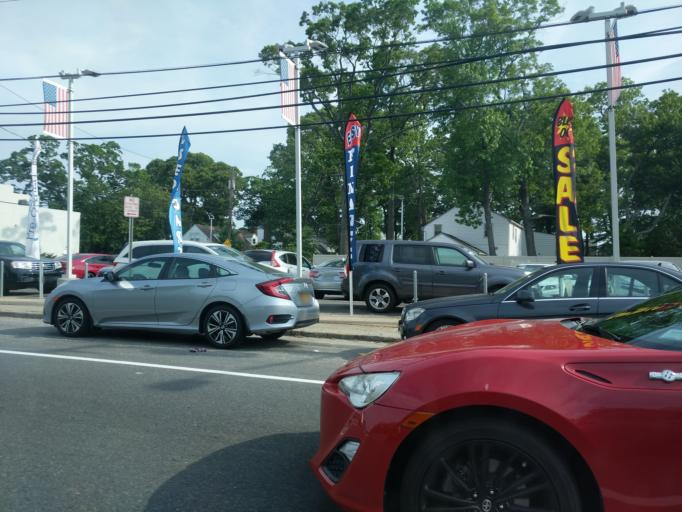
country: US
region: New York
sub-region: Nassau County
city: Hewlett
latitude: 40.6581
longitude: -73.6936
